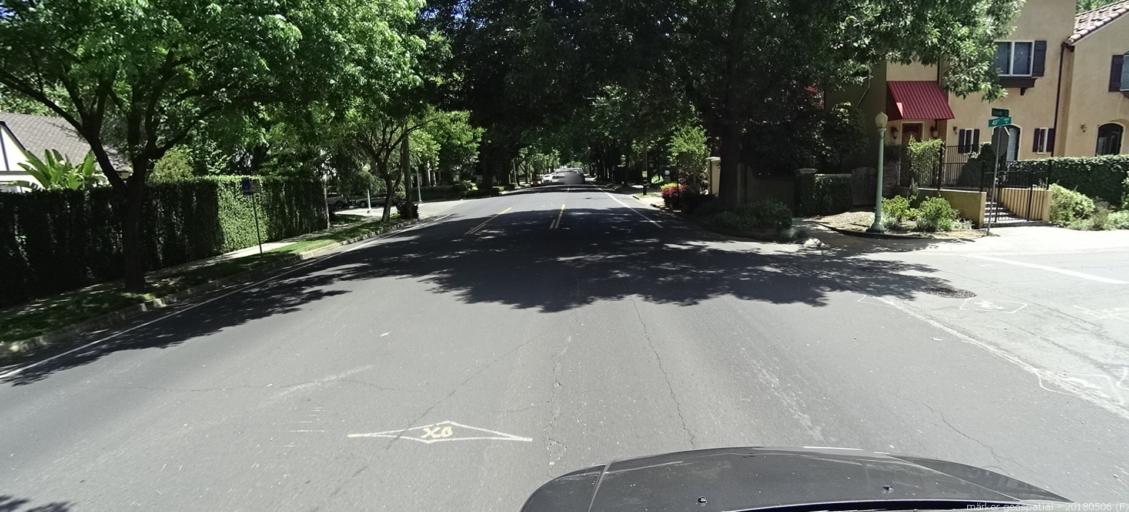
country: US
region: California
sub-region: Sacramento County
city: Sacramento
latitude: 38.5643
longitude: -121.4545
